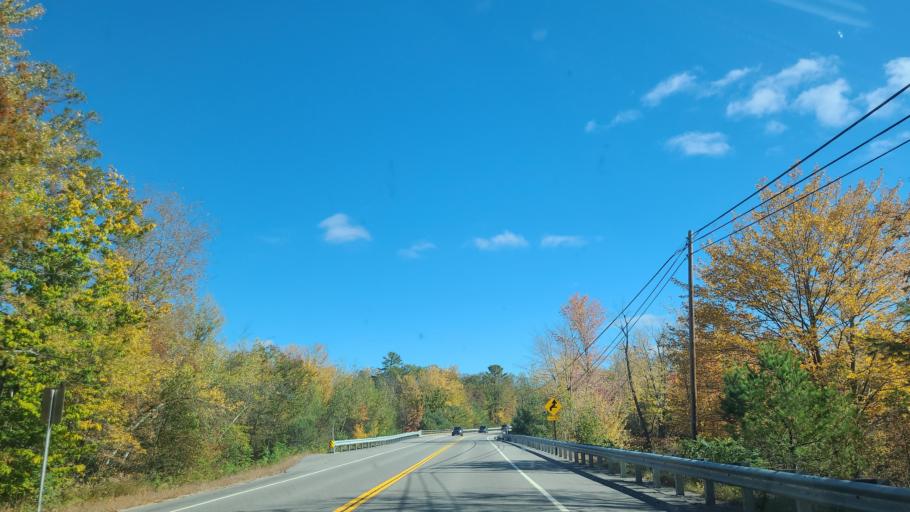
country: US
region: Maine
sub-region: Oxford County
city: Fryeburg
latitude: 44.0309
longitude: -70.9014
